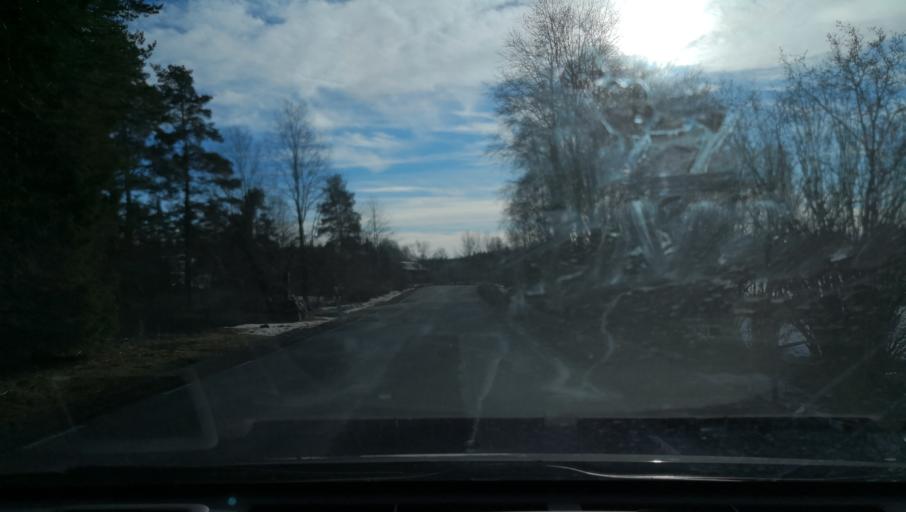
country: SE
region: Uppsala
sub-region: Osthammars Kommun
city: Osterbybruk
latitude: 60.2457
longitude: 17.9362
